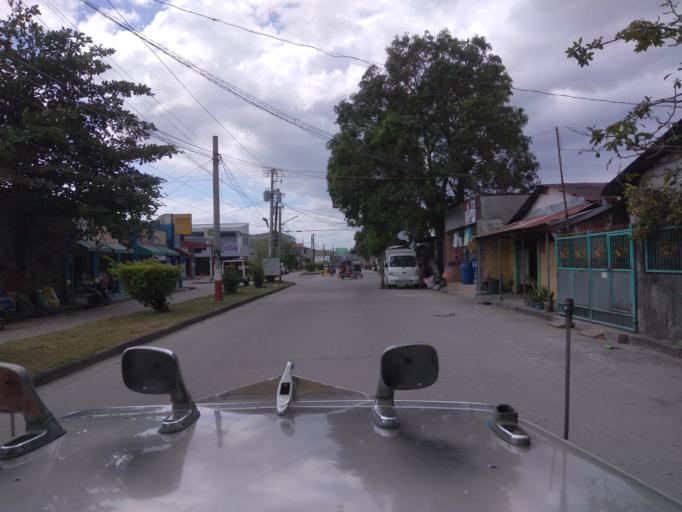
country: PH
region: Central Luzon
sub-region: Province of Pampanga
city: Pandacaqui
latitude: 15.1776
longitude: 120.6498
